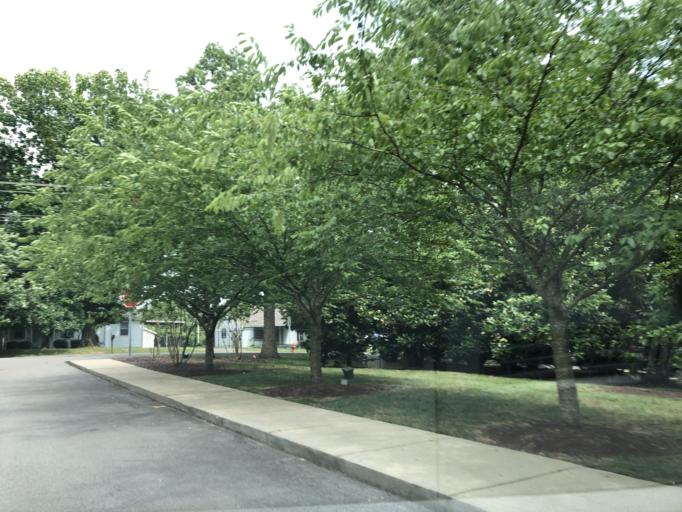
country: US
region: Tennessee
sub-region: Davidson County
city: Lakewood
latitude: 36.2648
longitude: -86.6918
